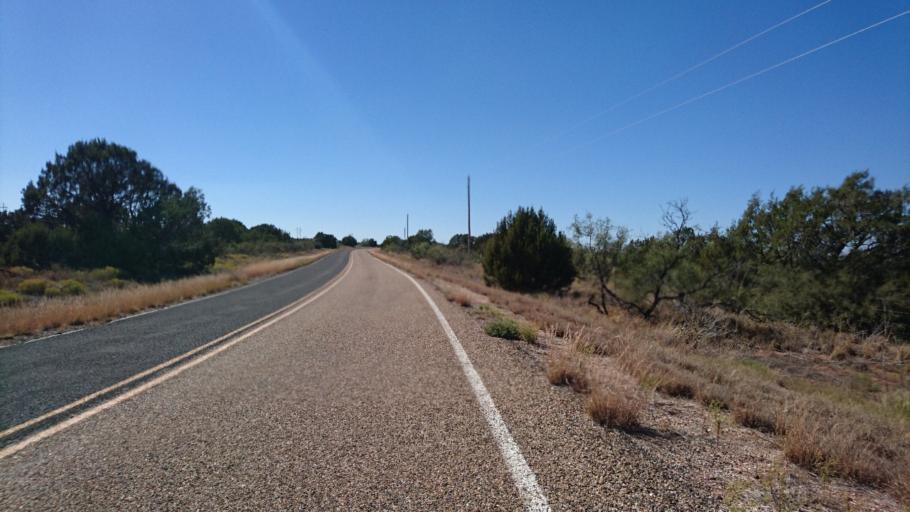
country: US
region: New Mexico
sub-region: Quay County
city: Tucumcari
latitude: 35.0674
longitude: -104.1818
